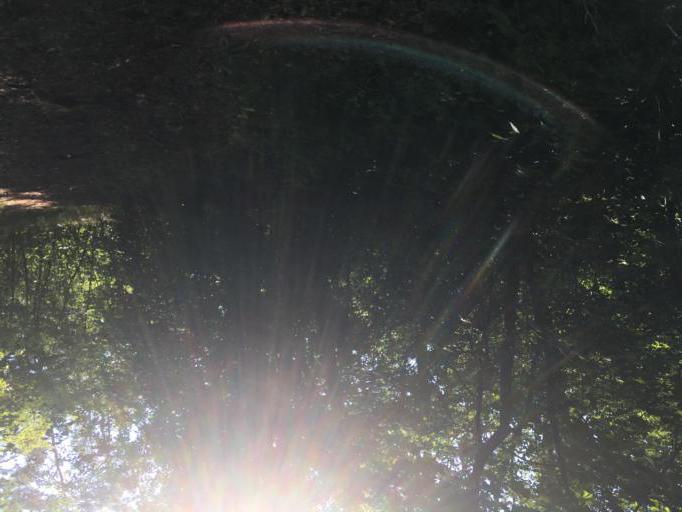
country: DE
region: Brandenburg
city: Templin
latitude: 53.1234
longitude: 13.5690
